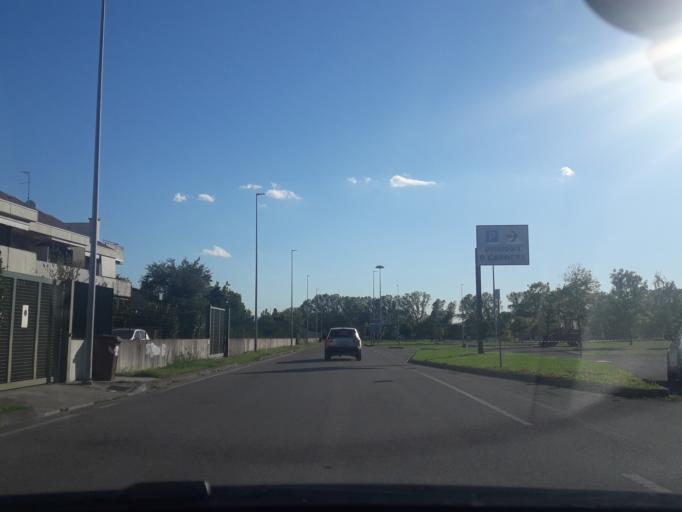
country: IT
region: Friuli Venezia Giulia
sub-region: Provincia di Udine
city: Colugna
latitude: 46.0814
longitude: 13.2033
